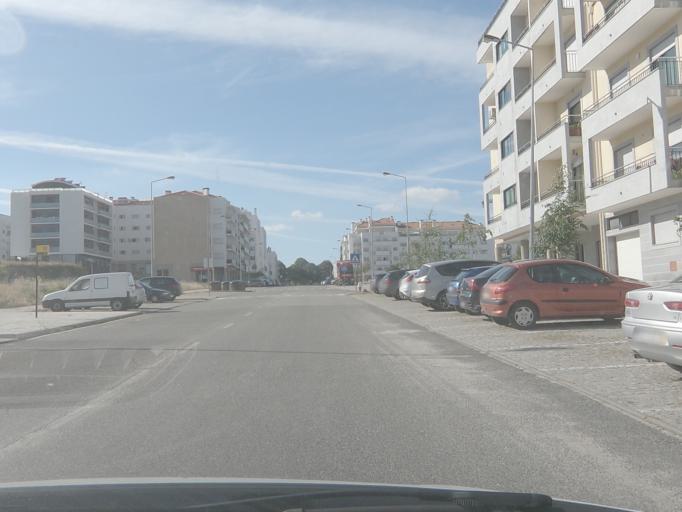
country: PT
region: Viseu
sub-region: Viseu
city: Viseu
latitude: 40.6449
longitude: -7.9095
